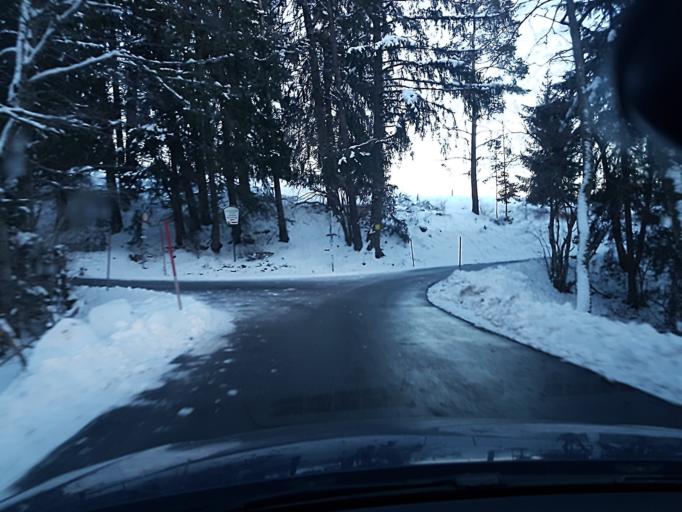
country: DE
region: Baden-Wuerttemberg
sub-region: Freiburg Region
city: Unterkirnach
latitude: 48.1105
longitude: 8.3618
